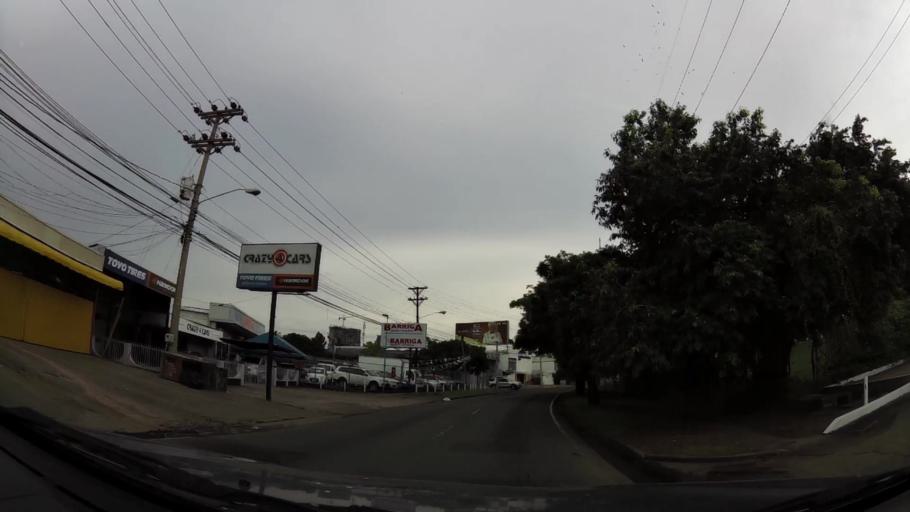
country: PA
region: Panama
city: Panama
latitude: 9.0090
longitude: -79.4975
